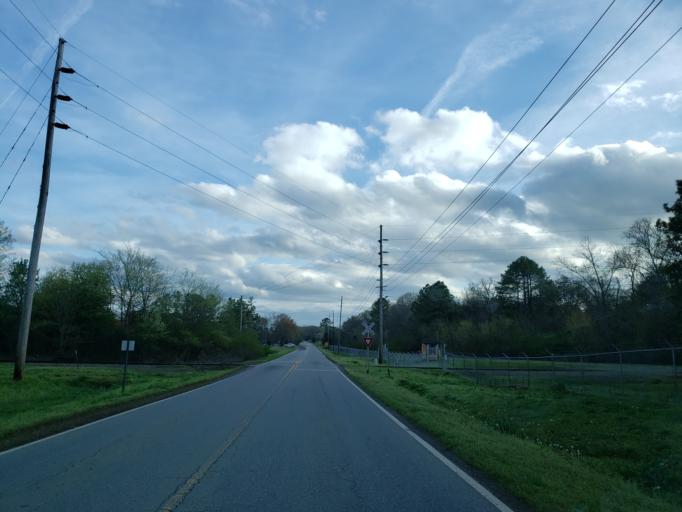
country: US
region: Georgia
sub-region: Bartow County
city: Cartersville
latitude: 34.2331
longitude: -84.8052
